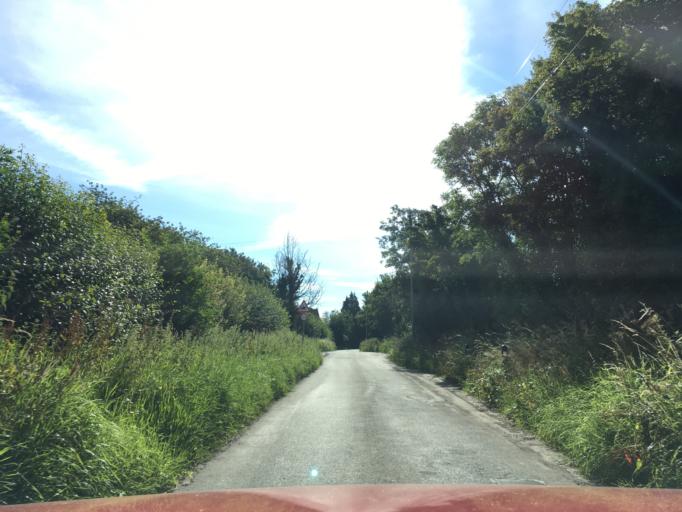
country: GB
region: England
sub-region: South Gloucestershire
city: Bitton
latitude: 51.4400
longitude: -2.4416
